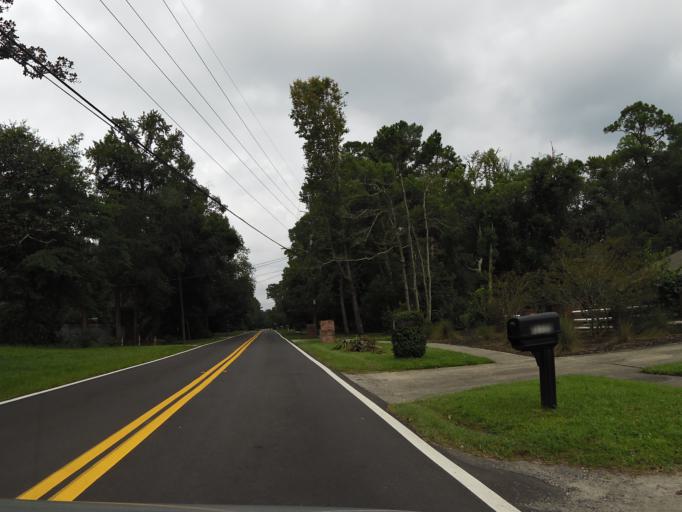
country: US
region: Florida
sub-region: Clay County
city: Bellair-Meadowbrook Terrace
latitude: 30.2512
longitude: -81.7163
